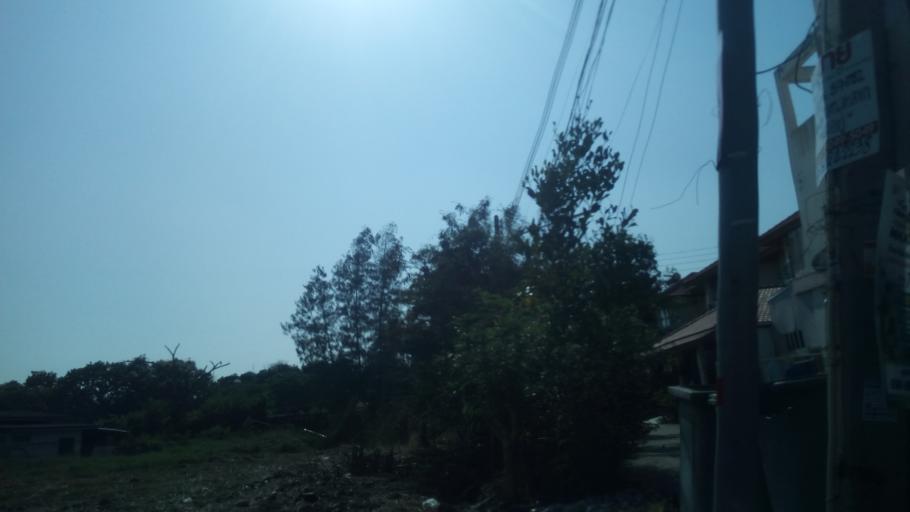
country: TH
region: Nakhon Pathom
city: Salaya
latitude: 13.8225
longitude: 100.3091
